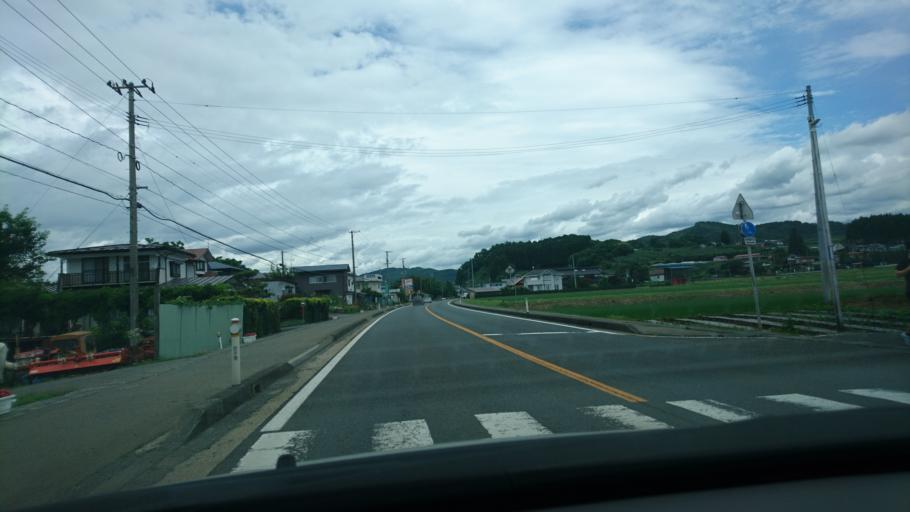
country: JP
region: Iwate
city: Morioka-shi
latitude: 39.6286
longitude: 141.1832
